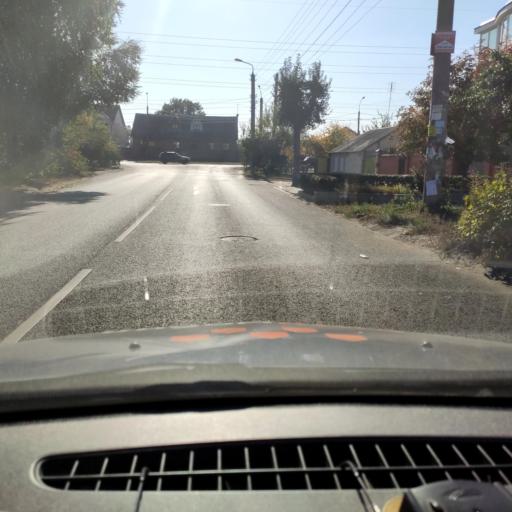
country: RU
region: Voronezj
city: Voronezh
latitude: 51.6385
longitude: 39.1671
